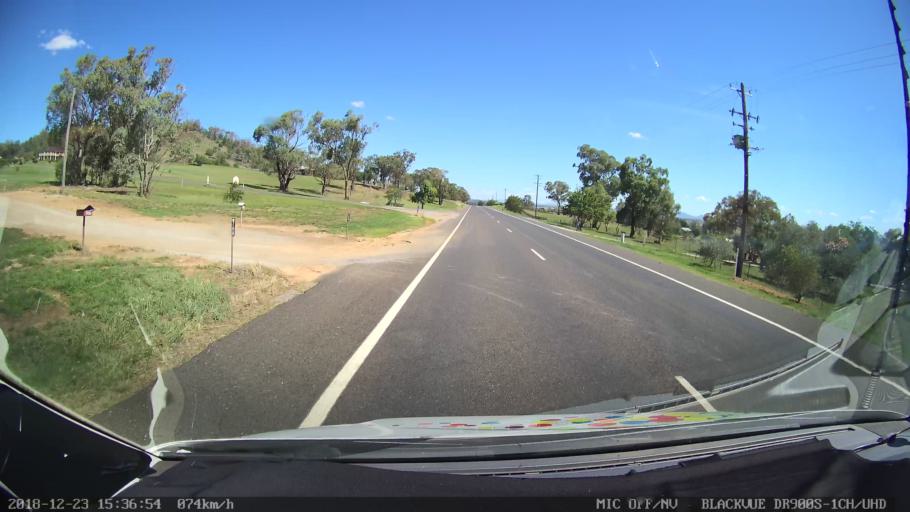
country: AU
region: New South Wales
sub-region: Tamworth Municipality
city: Tamworth
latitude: -31.0463
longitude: 150.8883
